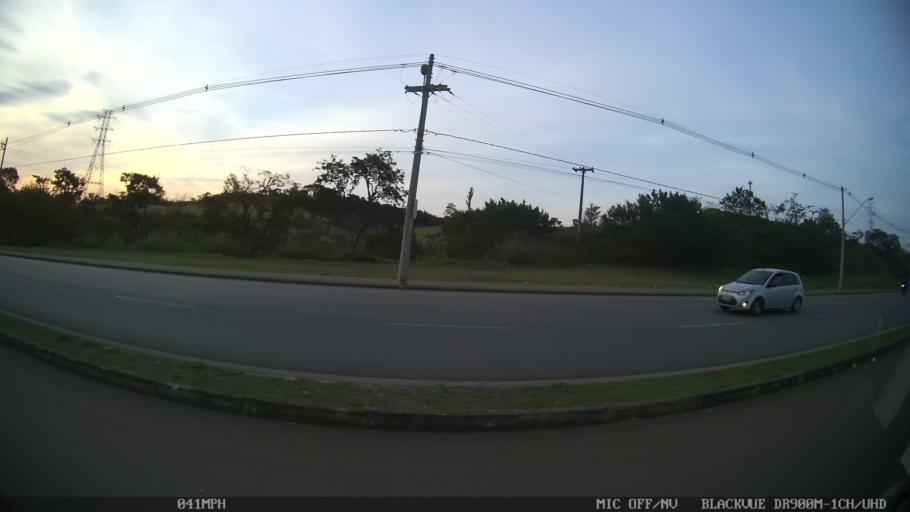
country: BR
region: Sao Paulo
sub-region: Limeira
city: Limeira
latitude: -22.5429
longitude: -47.4064
